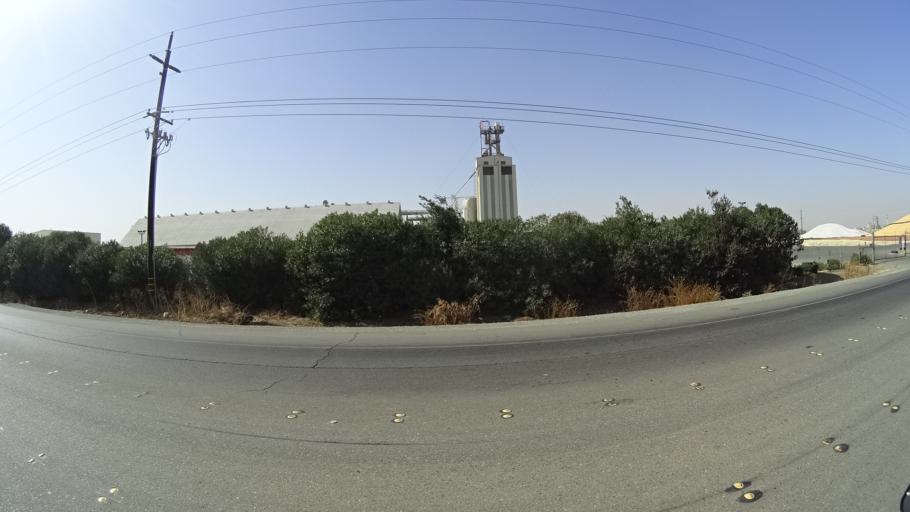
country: US
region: California
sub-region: Yolo County
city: Woodland
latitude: 38.6792
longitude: -121.7284
